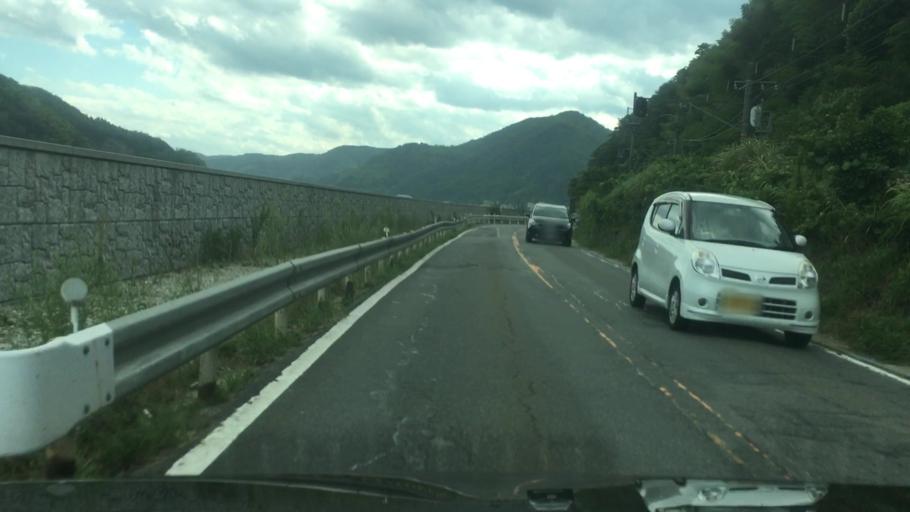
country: JP
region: Hyogo
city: Toyooka
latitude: 35.6139
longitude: 134.8080
